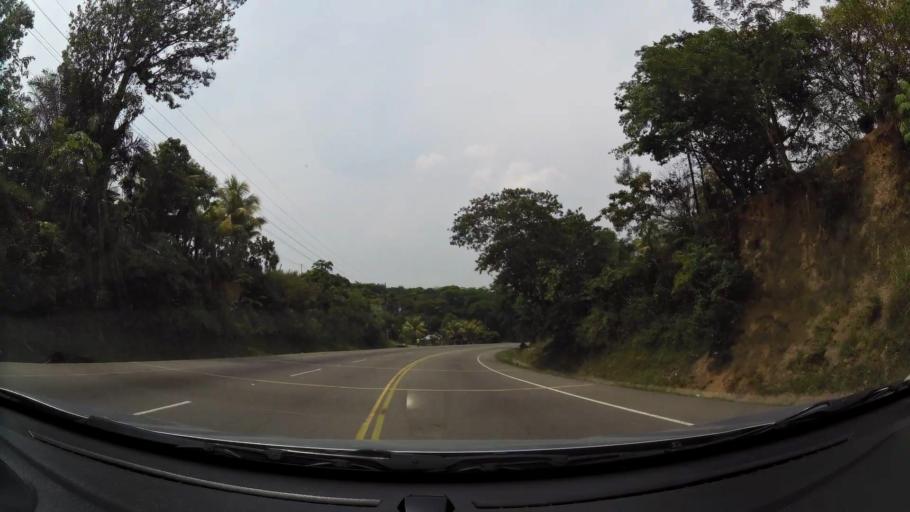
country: HN
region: Cortes
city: Santa Cruz de Yojoa
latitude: 14.9821
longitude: -87.9309
